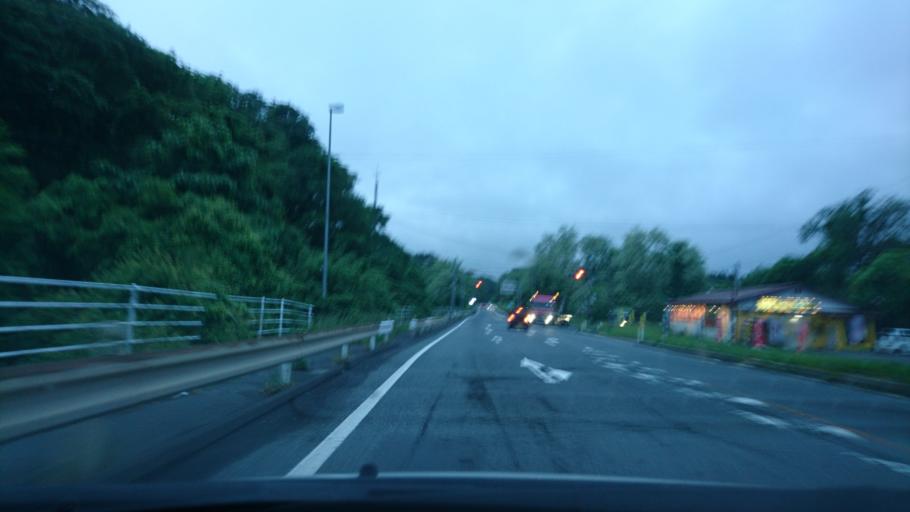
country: JP
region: Iwate
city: Ichinoseki
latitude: 38.8782
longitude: 141.1184
